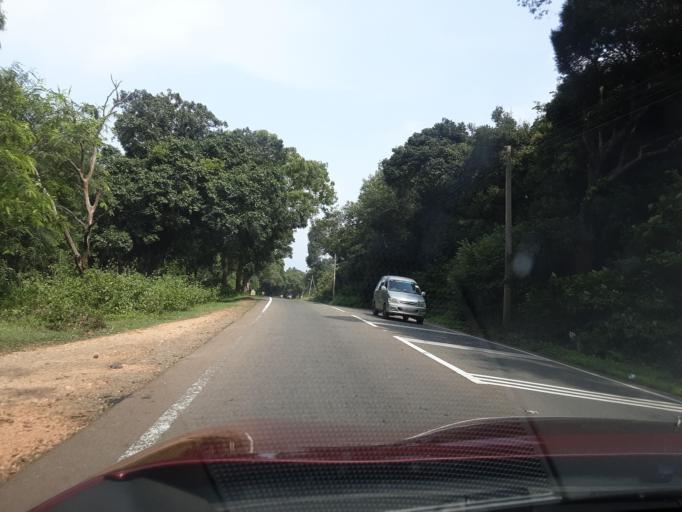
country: LK
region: North Central
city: Anuradhapura
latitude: 8.3487
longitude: 80.5081
